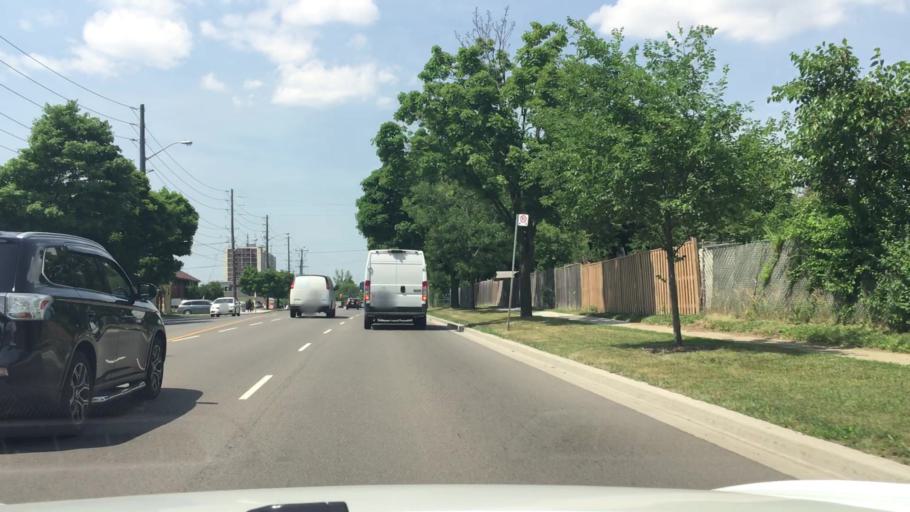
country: CA
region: Ontario
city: Scarborough
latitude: 43.7781
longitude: -79.2967
